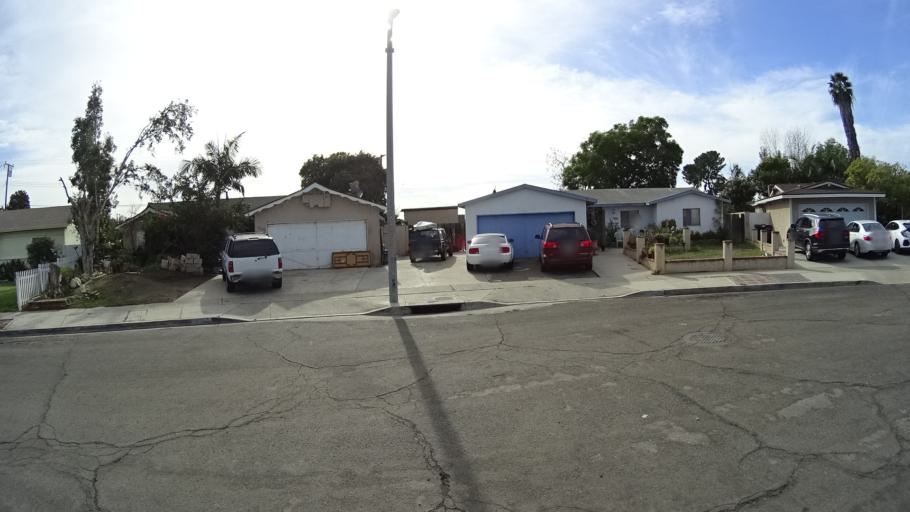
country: US
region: California
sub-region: Orange County
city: Garden Grove
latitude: 33.7804
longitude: -117.9089
